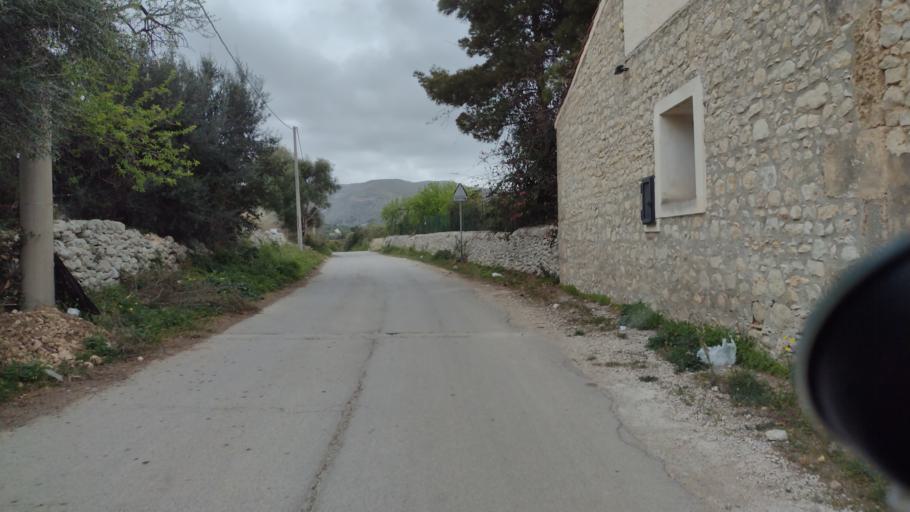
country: IT
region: Sicily
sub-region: Provincia di Siracusa
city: Avola
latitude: 36.9096
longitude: 15.1157
